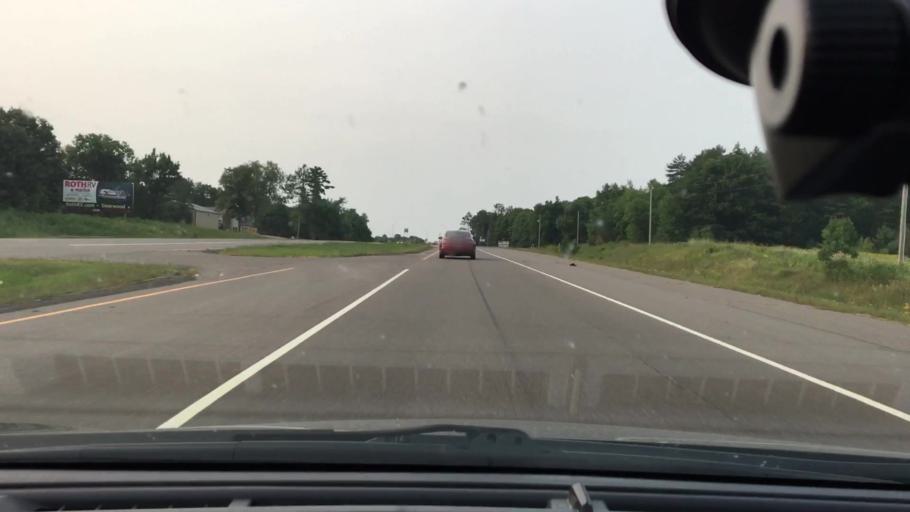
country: US
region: Minnesota
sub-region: Mille Lacs County
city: Vineland
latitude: 46.1016
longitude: -93.6445
